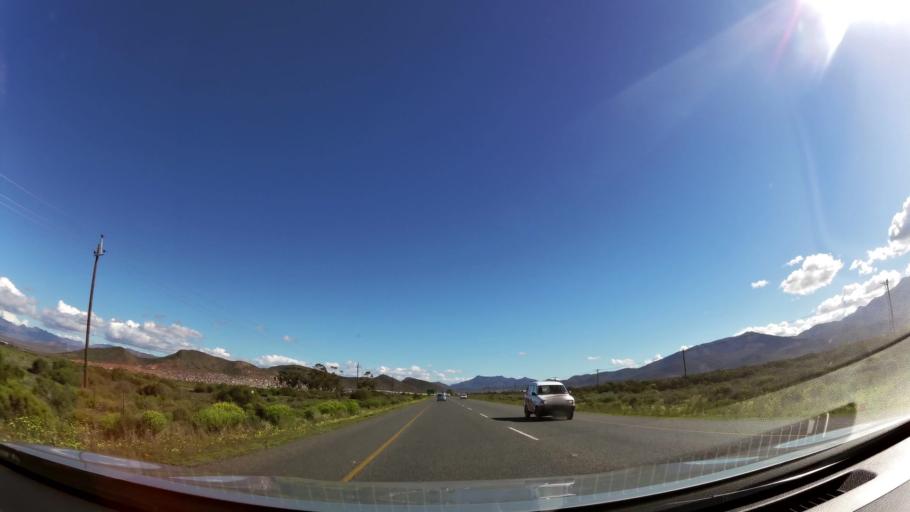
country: ZA
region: Western Cape
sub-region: Cape Winelands District Municipality
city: Ashton
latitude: -33.8146
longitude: 19.9132
